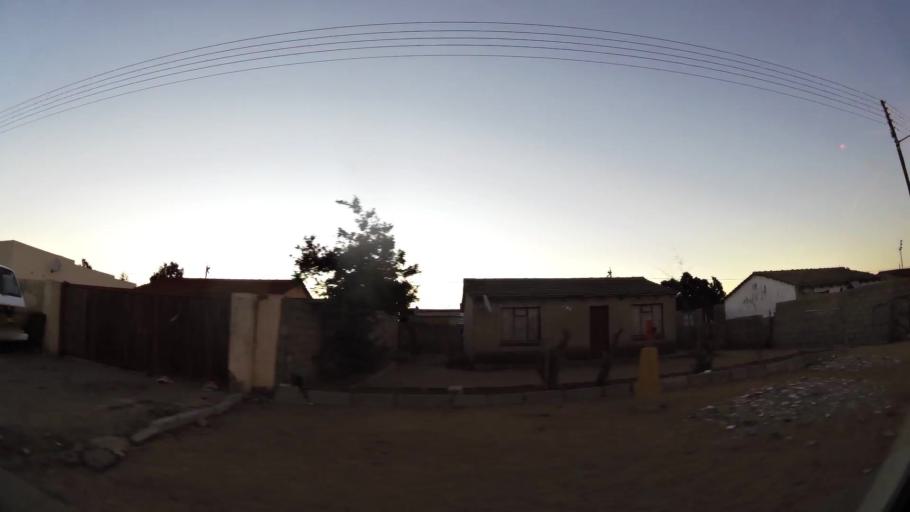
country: ZA
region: Limpopo
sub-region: Capricorn District Municipality
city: Polokwane
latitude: -23.8567
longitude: 29.3878
